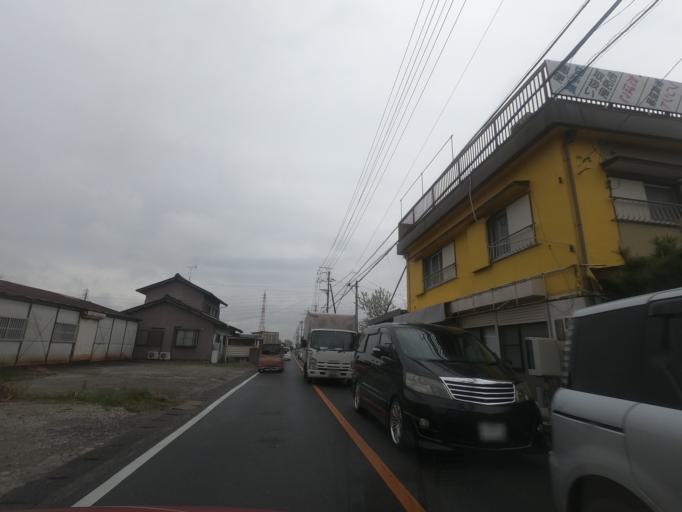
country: JP
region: Aichi
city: Kasugai
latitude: 35.2484
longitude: 137.0014
